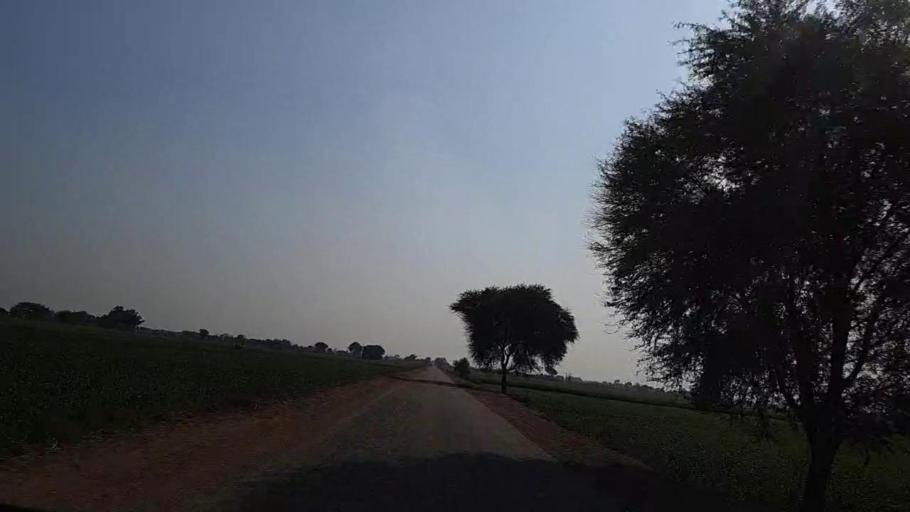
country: PK
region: Sindh
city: Sakrand
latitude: 26.0873
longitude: 68.2902
